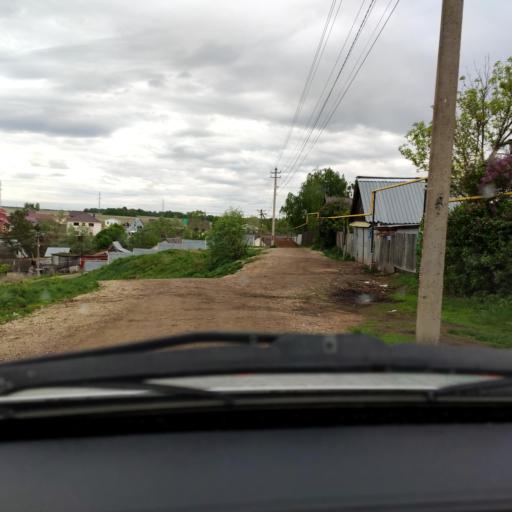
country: RU
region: Bashkortostan
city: Mikhaylovka
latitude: 54.8149
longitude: 55.8500
